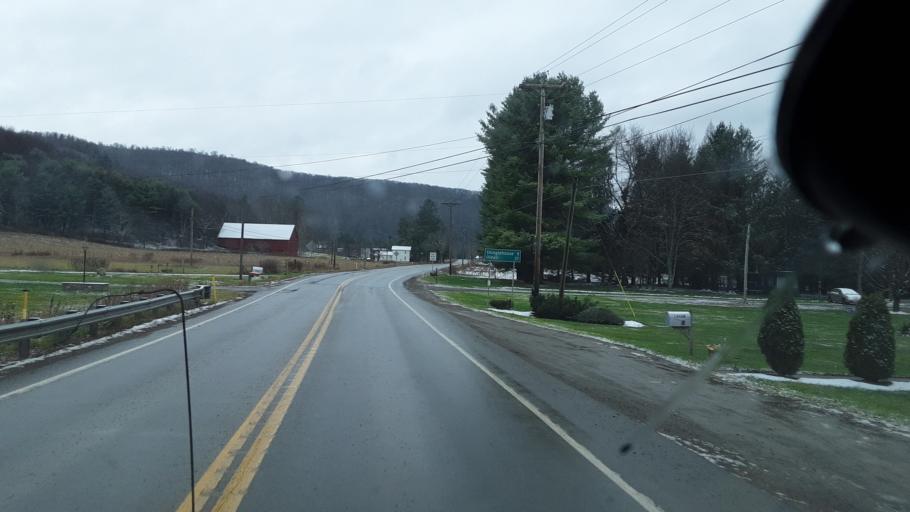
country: US
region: Pennsylvania
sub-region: Potter County
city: Coudersport
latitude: 41.9027
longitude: -78.0670
